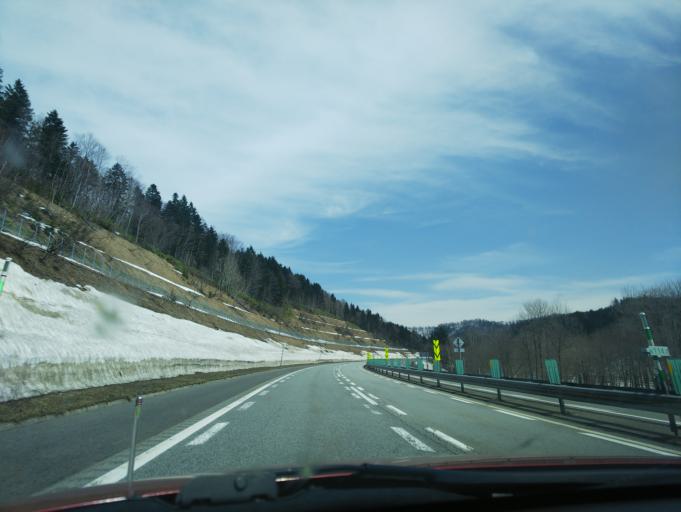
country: JP
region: Hokkaido
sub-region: Asahikawa-shi
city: Asahikawa
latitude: 43.7801
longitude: 142.1974
